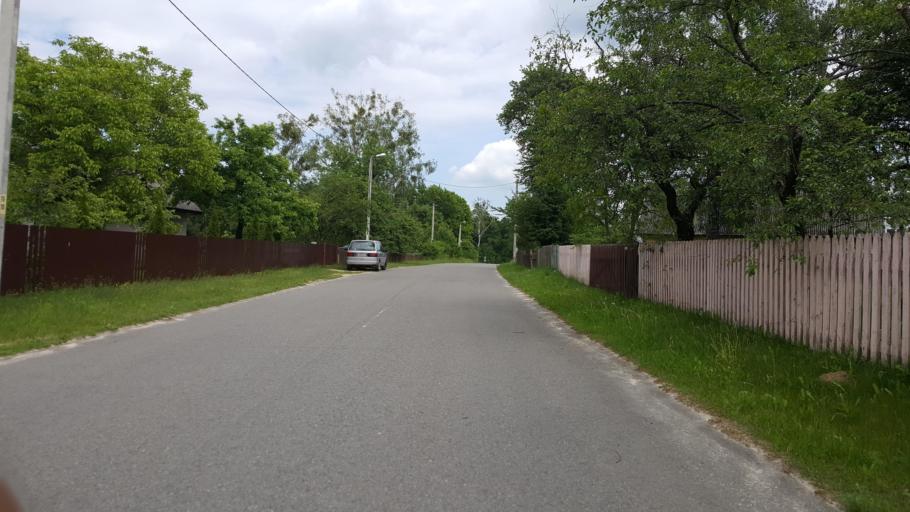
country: PL
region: Podlasie
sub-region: Powiat hajnowski
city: Bialowieza
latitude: 52.6255
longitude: 24.0722
